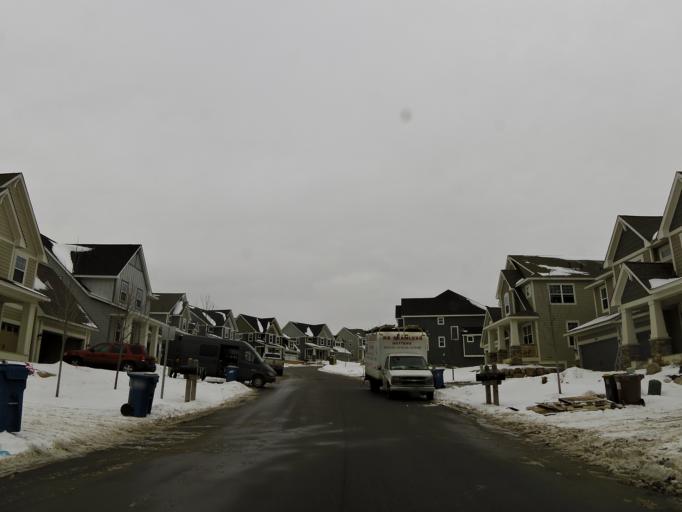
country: US
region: Minnesota
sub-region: Dakota County
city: Inver Grove Heights
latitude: 44.8389
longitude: -93.0915
